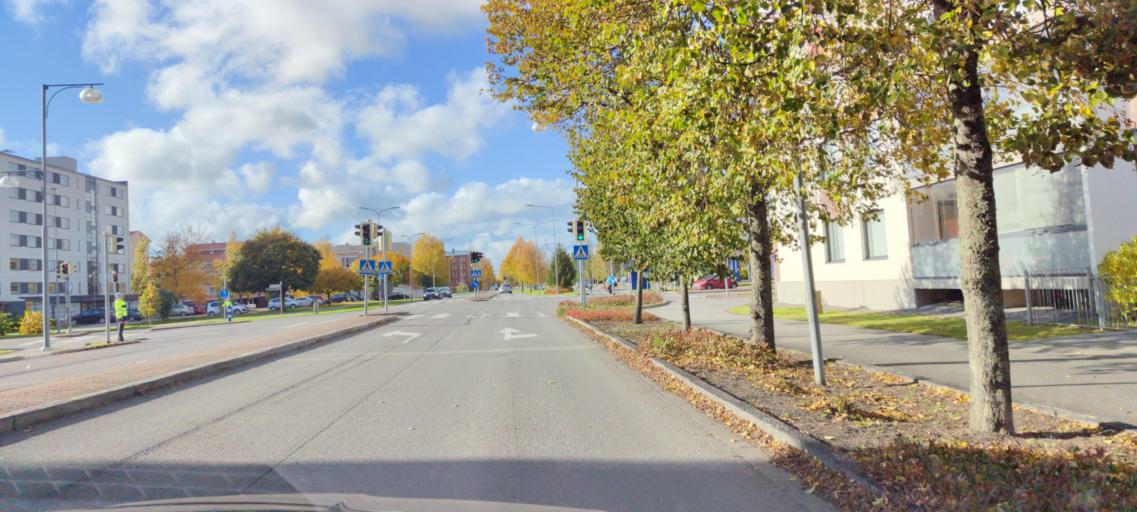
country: FI
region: Varsinais-Suomi
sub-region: Turku
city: Kaarina
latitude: 60.4071
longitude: 22.3639
